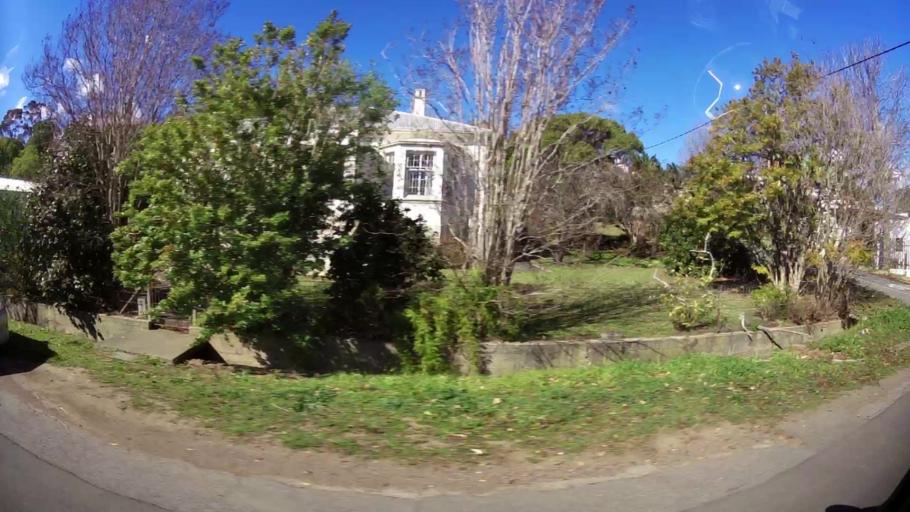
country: ZA
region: Western Cape
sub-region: Overberg District Municipality
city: Swellendam
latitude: -34.0236
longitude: 20.4472
